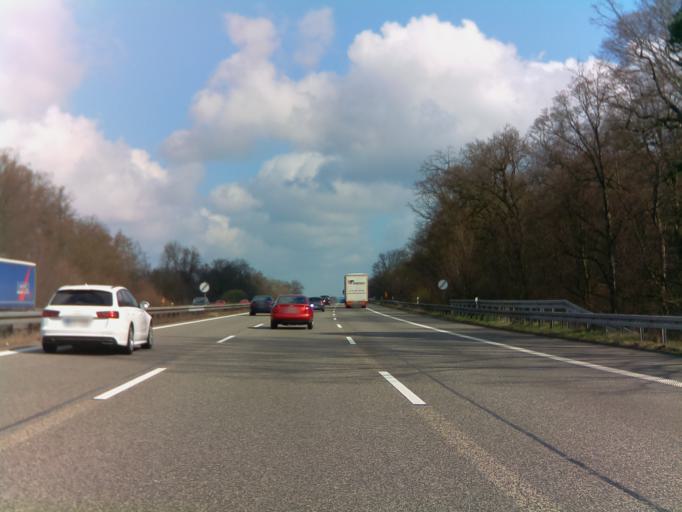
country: DE
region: Saxony-Anhalt
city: Dessau
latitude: 51.7905
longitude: 12.2737
